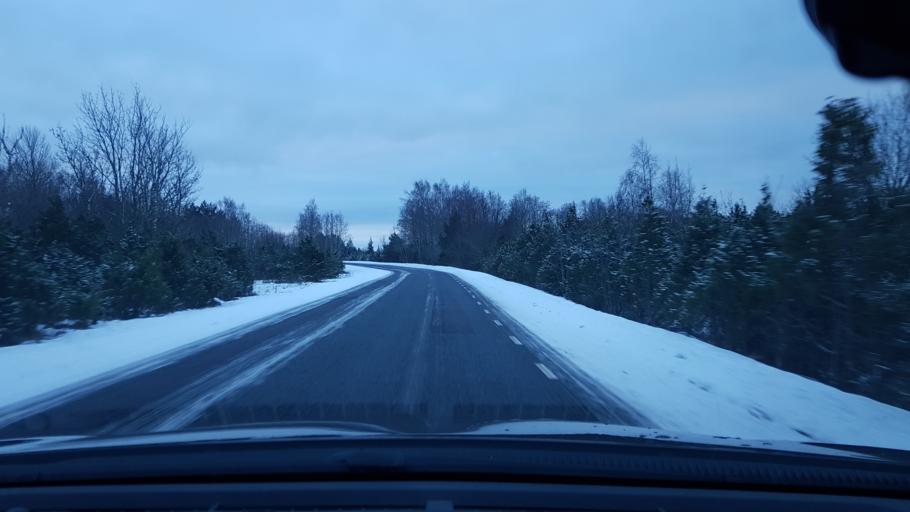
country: EE
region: Laeaene
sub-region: Haapsalu linn
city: Haapsalu
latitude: 59.1171
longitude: 23.5337
